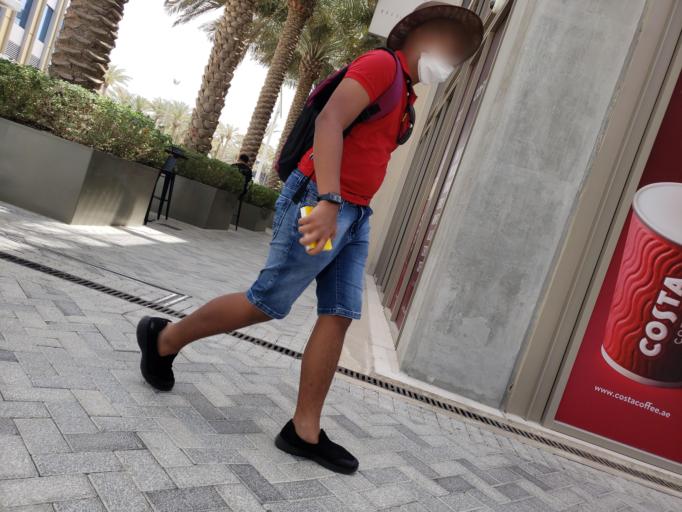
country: AE
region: Dubai
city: Dubai
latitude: 24.9602
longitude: 55.1497
